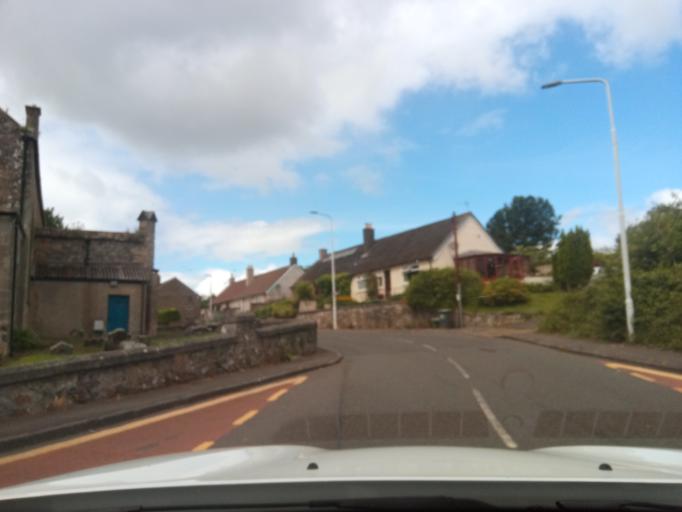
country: GB
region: Scotland
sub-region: Fife
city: Oakley
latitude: 56.0579
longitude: -3.5651
